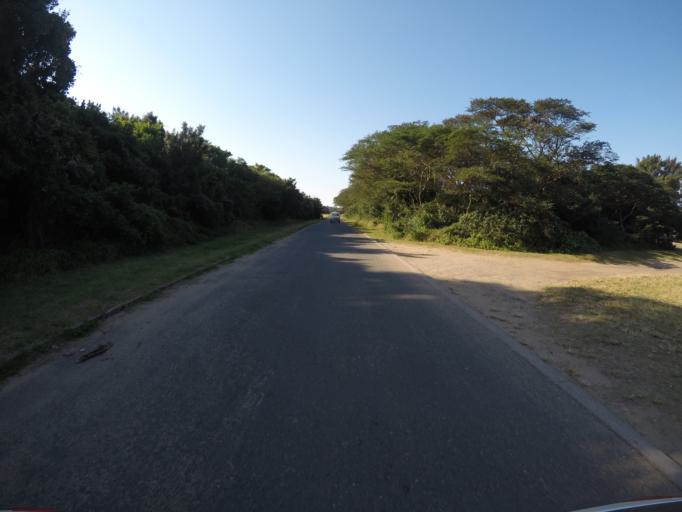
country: ZA
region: KwaZulu-Natal
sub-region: uThungulu District Municipality
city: Richards Bay
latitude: -28.8011
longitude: 32.0806
